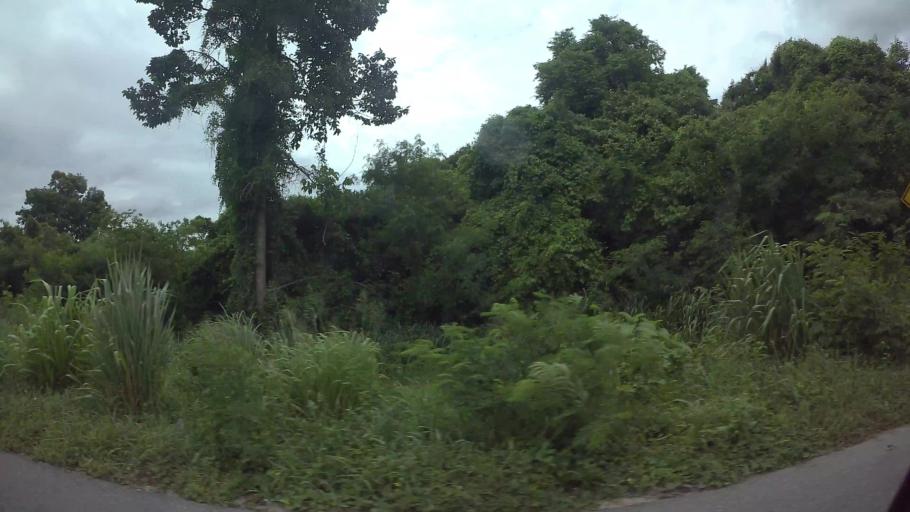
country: TH
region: Chon Buri
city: Si Racha
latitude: 13.1781
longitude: 100.9717
